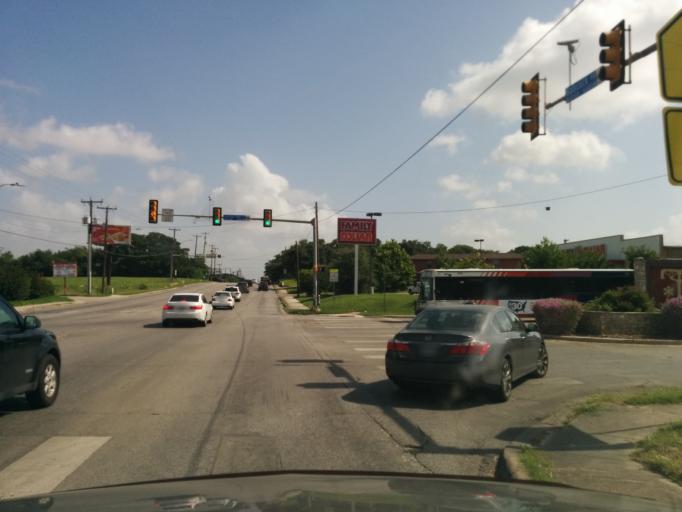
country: US
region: Texas
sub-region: Bexar County
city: Leon Valley
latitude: 29.5520
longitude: -98.6149
